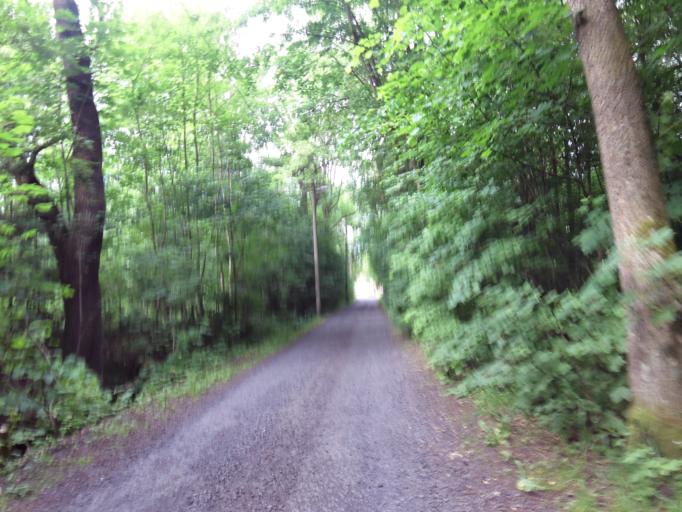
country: CZ
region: Ustecky
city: Dolni Podluzi
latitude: 50.8934
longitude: 14.6094
